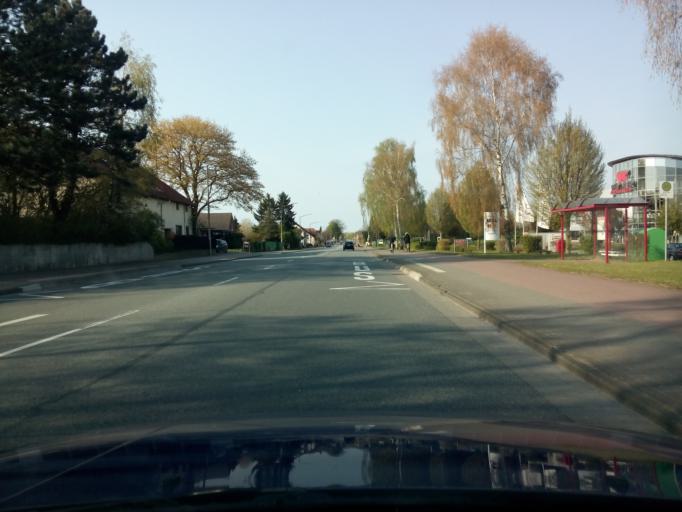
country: DE
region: Lower Saxony
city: Syke
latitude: 52.9311
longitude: 8.8247
